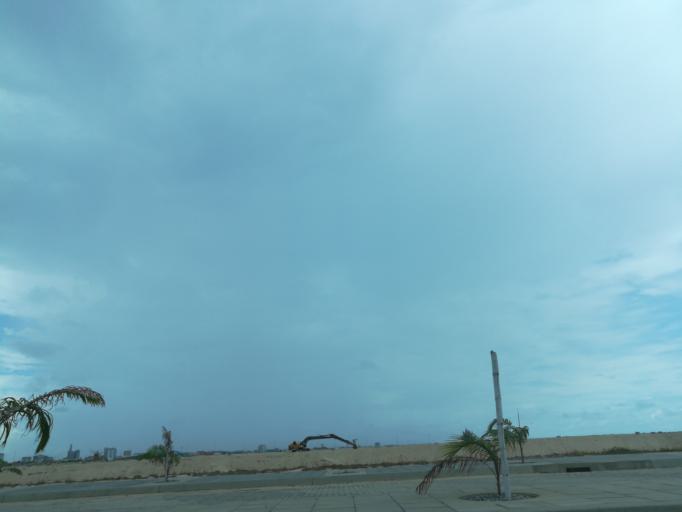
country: NG
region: Lagos
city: Ikoyi
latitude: 6.4076
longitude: 3.4207
